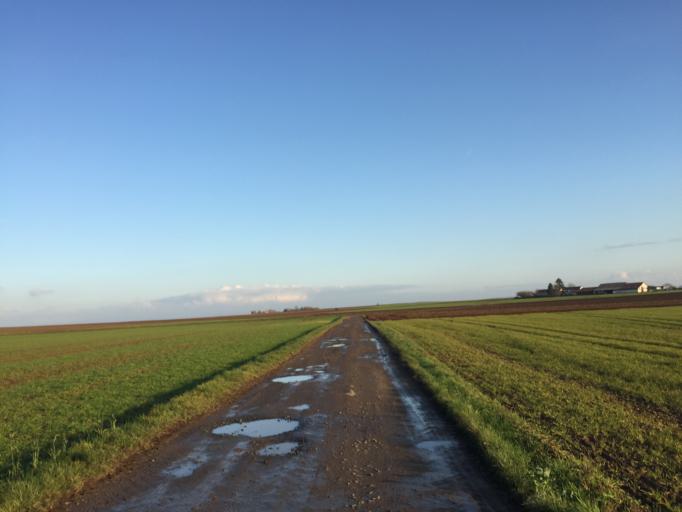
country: DE
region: Hesse
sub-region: Regierungsbezirk Darmstadt
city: Munzenberg
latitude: 50.4849
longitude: 8.7385
